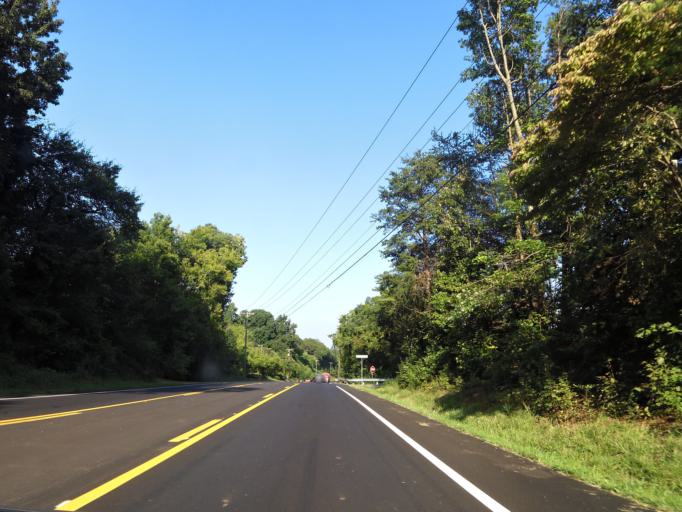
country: US
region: Tennessee
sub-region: Knox County
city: Knoxville
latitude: 35.8888
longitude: -83.9340
